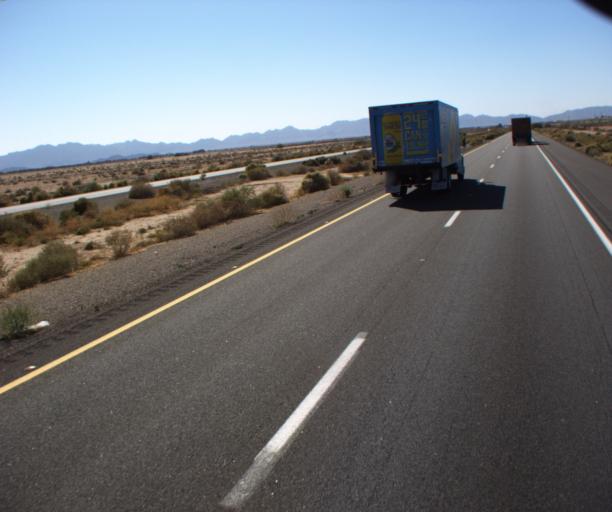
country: US
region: Arizona
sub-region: Yuma County
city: Wellton
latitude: 32.6744
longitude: -114.0752
